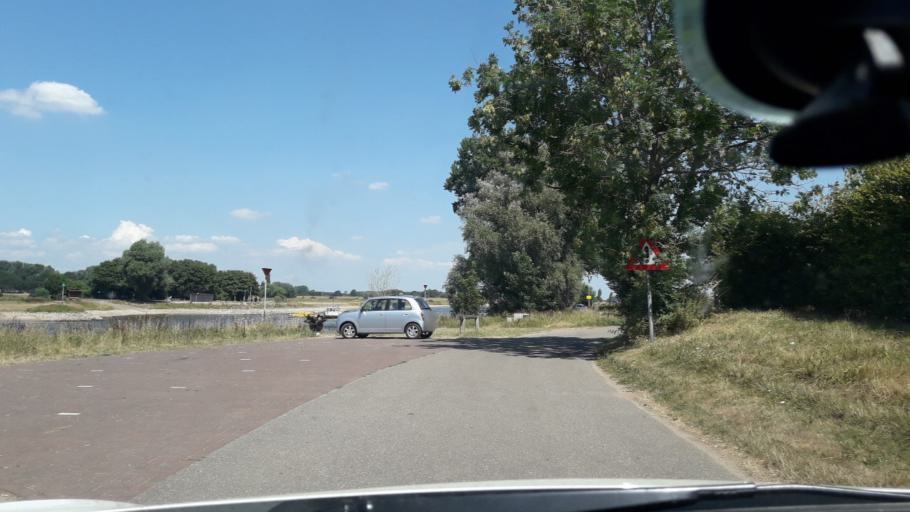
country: NL
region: Gelderland
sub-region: Gemeente Brummen
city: Brummen
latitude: 52.0805
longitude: 6.1726
